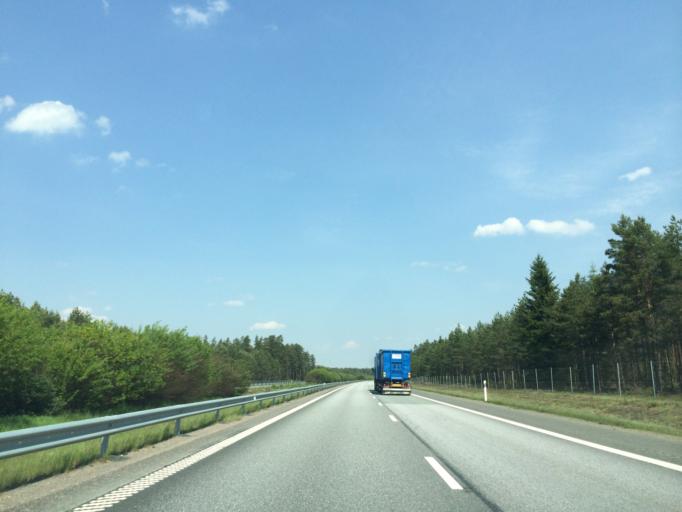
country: SE
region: Joenkoeping
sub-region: Varnamo Kommun
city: Varnamo
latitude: 57.2816
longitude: 14.0831
